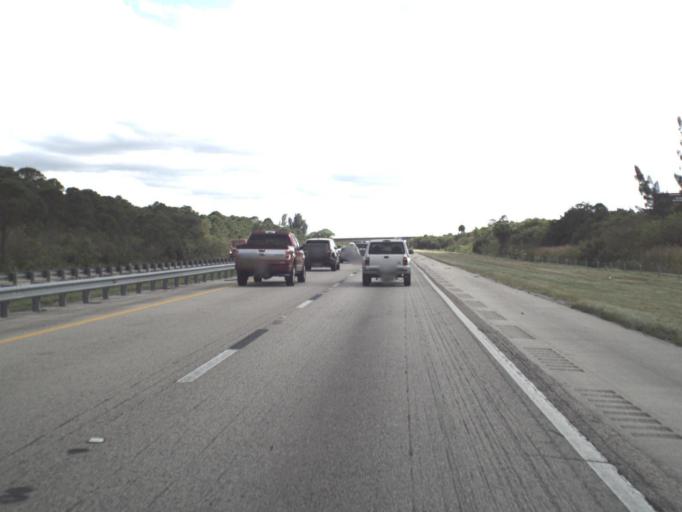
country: US
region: Florida
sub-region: Saint Lucie County
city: Lakewood Park
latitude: 27.4528
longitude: -80.4289
